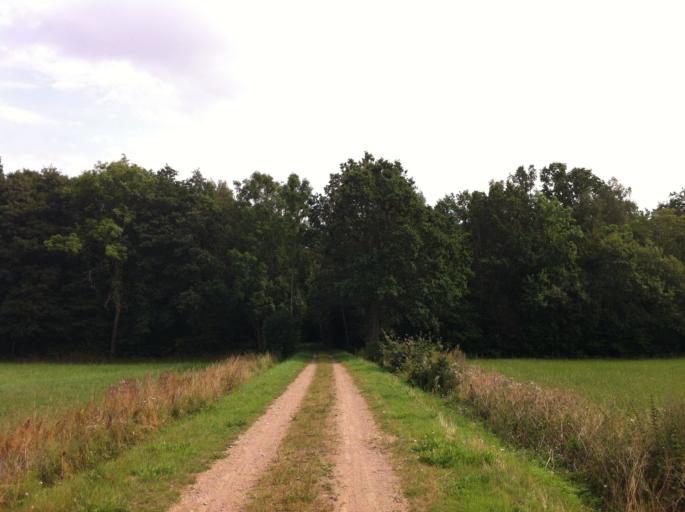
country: SE
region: Skane
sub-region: Kristianstads Kommun
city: Onnestad
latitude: 55.9435
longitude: 13.9048
